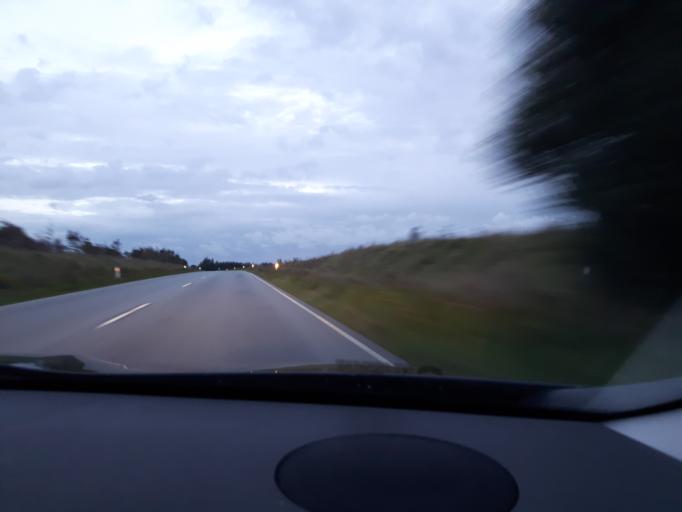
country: DK
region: North Denmark
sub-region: Hjorring Kommune
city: Hjorring
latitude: 57.5073
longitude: 9.9459
